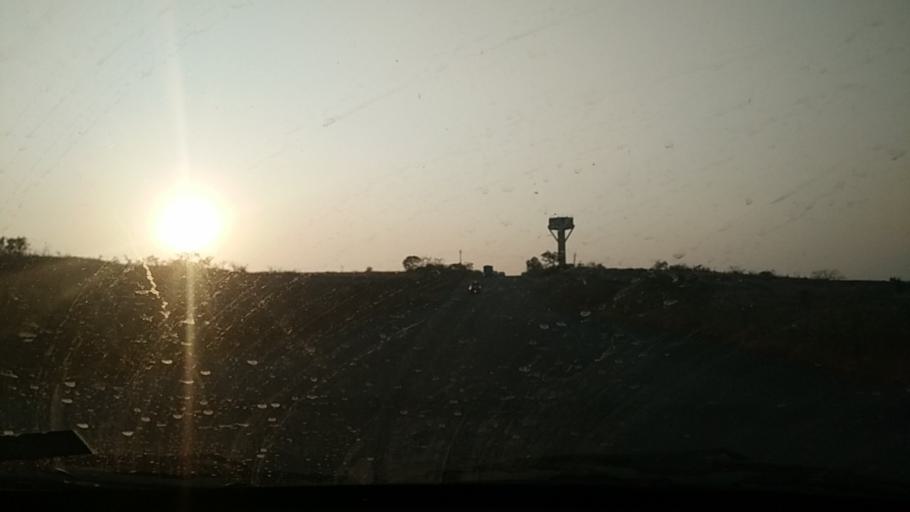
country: IN
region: Goa
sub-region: North Goa
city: Queula
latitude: 15.3559
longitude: 73.9571
